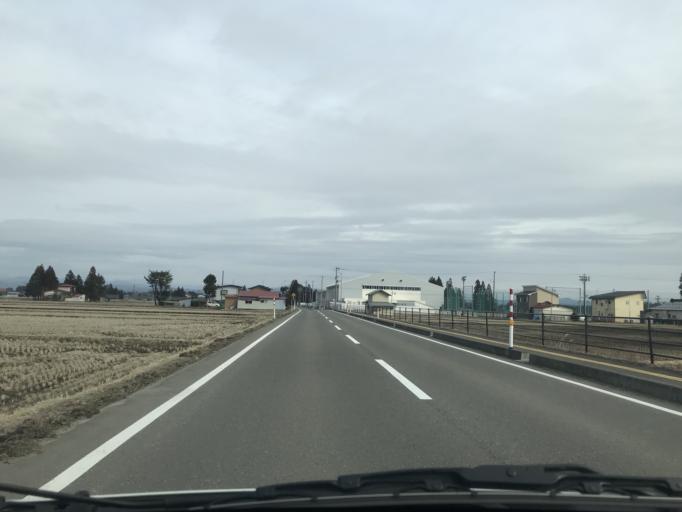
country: JP
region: Iwate
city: Hanamaki
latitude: 39.3641
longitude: 141.0513
